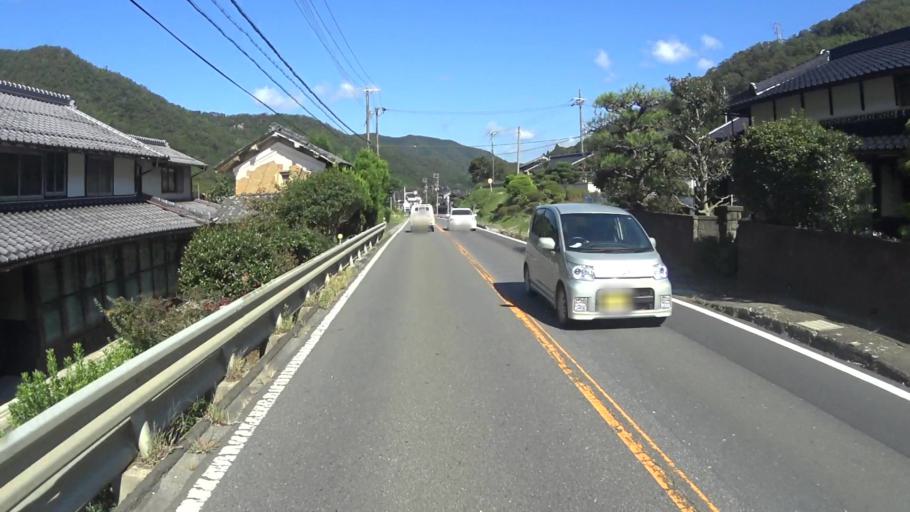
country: JP
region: Kyoto
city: Ayabe
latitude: 35.2305
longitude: 135.4150
